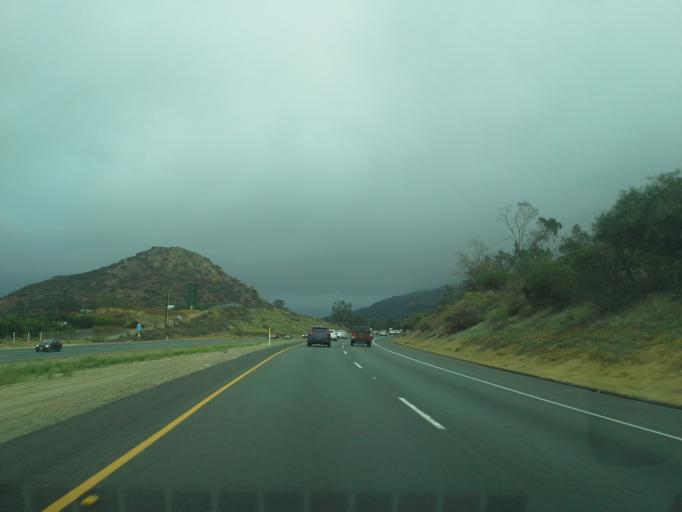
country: US
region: California
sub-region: San Diego County
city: Harbison Canyon
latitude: 32.8541
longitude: -116.8610
